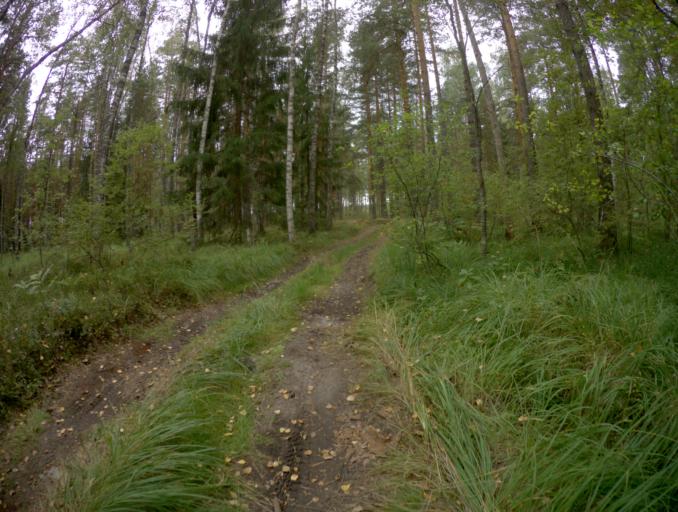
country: RU
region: Vladimir
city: Ivanishchi
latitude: 55.8445
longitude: 40.3408
